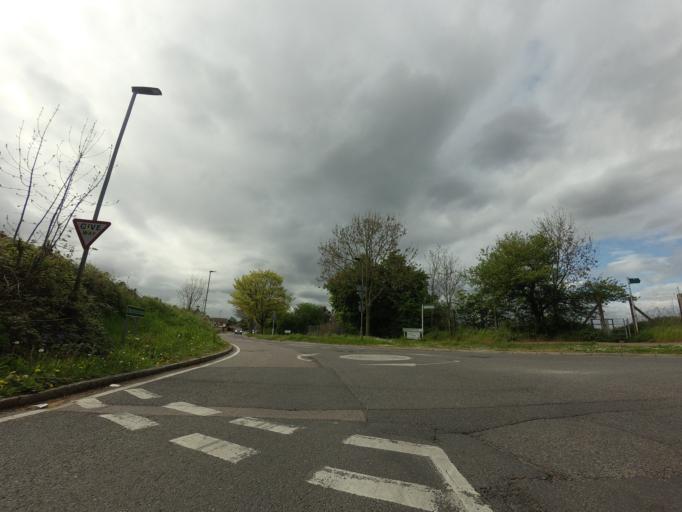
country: GB
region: England
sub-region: Greater London
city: Orpington
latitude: 51.3828
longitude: 0.1193
